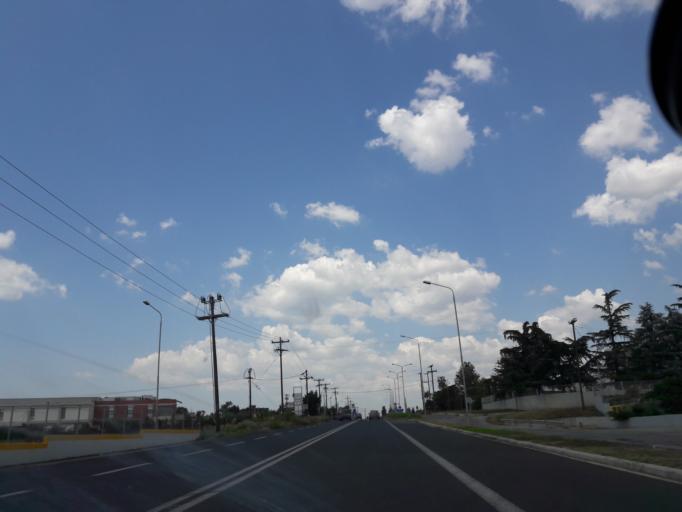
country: GR
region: Central Macedonia
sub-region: Nomos Thessalonikis
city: Thermi
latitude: 40.5300
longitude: 23.0430
